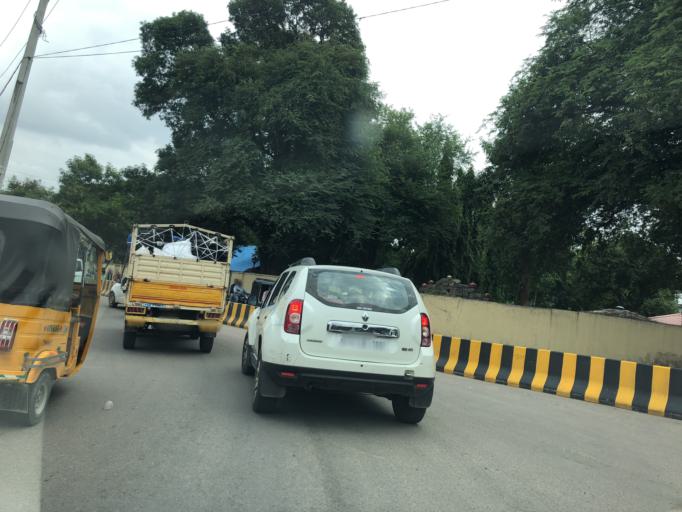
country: IN
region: Telangana
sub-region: Rangareddi
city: Quthbullapur
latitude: 17.4700
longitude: 78.4763
